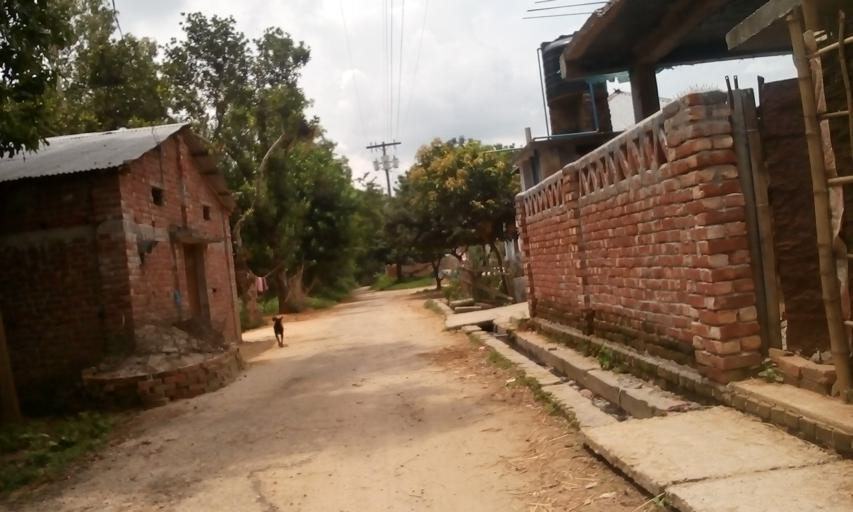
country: BD
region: Rangpur Division
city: Parbatipur
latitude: 25.4007
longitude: 88.9898
